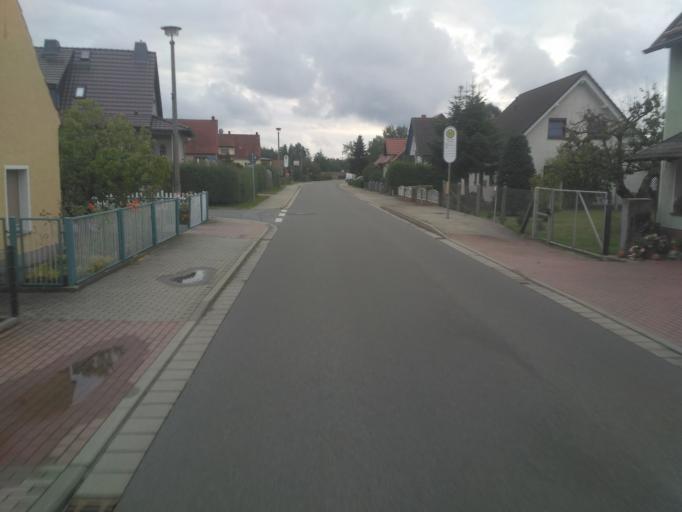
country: DE
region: Saxony
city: Wittichenau
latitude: 51.3777
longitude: 14.2552
